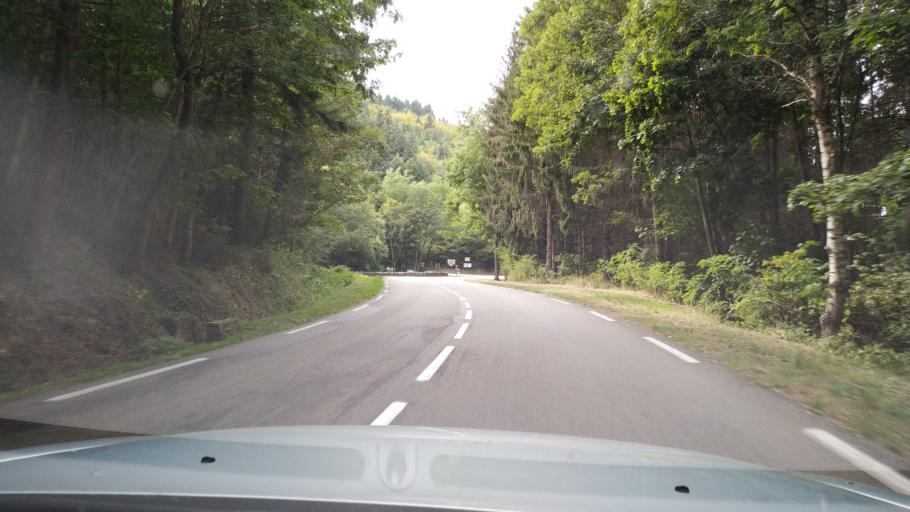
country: FR
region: Rhone-Alpes
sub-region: Departement de l'Ardeche
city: Desaignes
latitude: 44.9862
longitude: 4.5373
